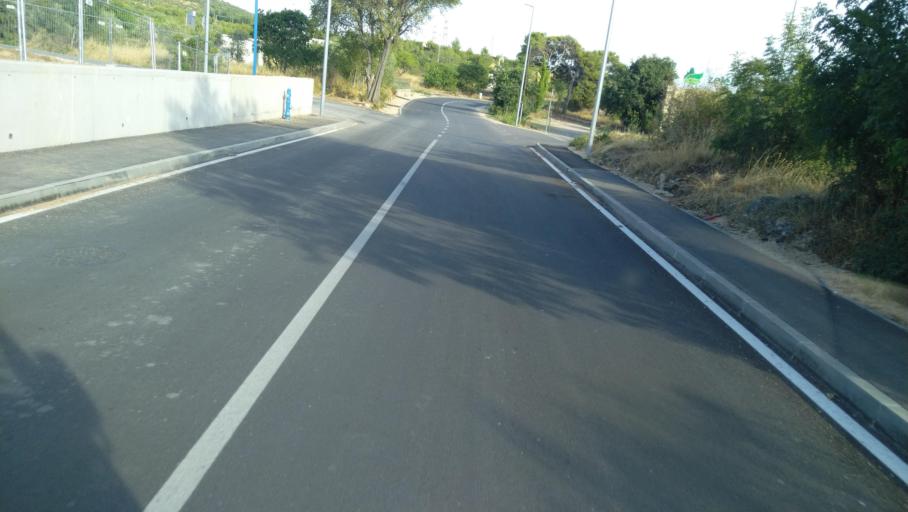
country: HR
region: Sibensko-Kniniska
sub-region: Grad Sibenik
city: Sibenik
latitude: 43.7187
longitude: 15.9127
